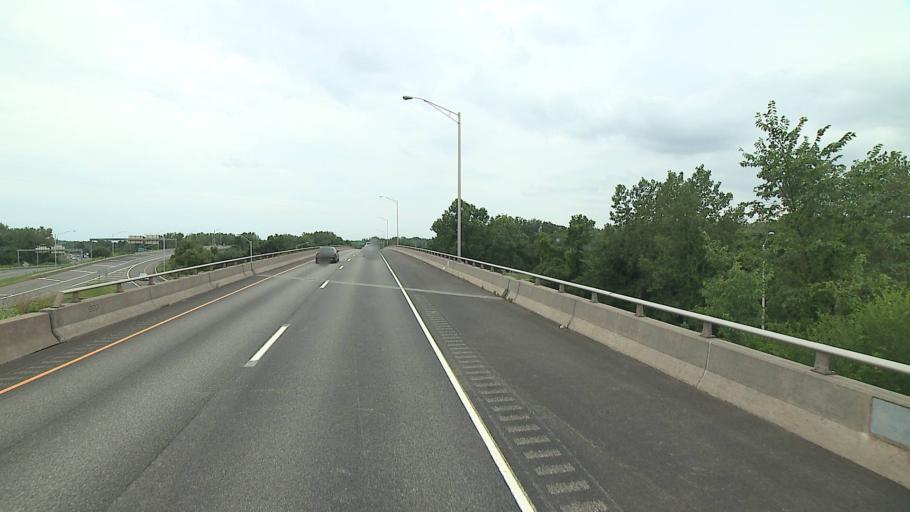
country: US
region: Connecticut
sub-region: Hartford County
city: Wethersfield
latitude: 41.7100
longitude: -72.6445
